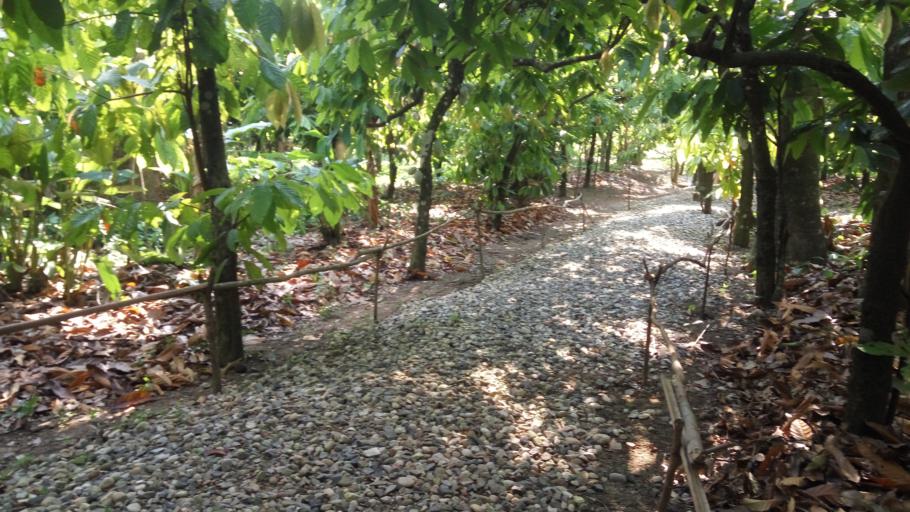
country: MX
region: Tabasco
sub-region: Cunduacan
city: Cumuapa 1ra. Seccion
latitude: 17.9786
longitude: -93.1317
